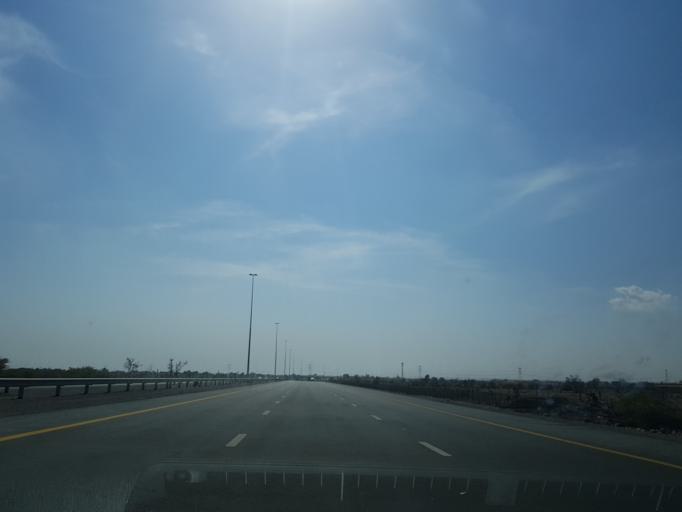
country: AE
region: Ra's al Khaymah
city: Ras al-Khaimah
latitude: 25.7068
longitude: 55.9973
